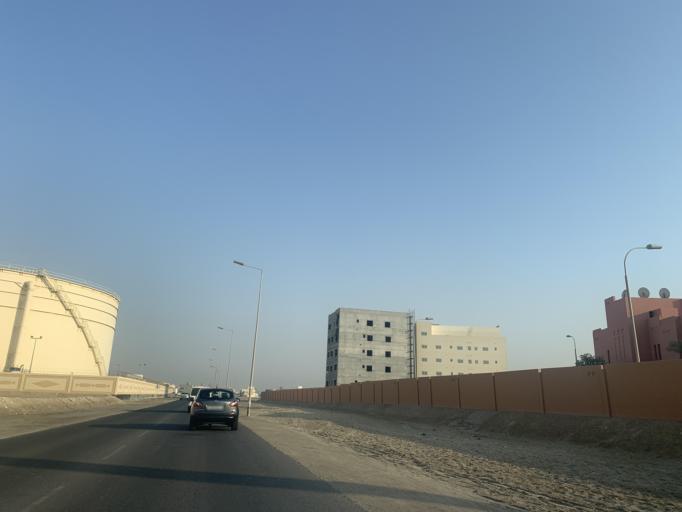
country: BH
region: Manama
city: Jidd Hafs
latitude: 26.2094
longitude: 50.5249
